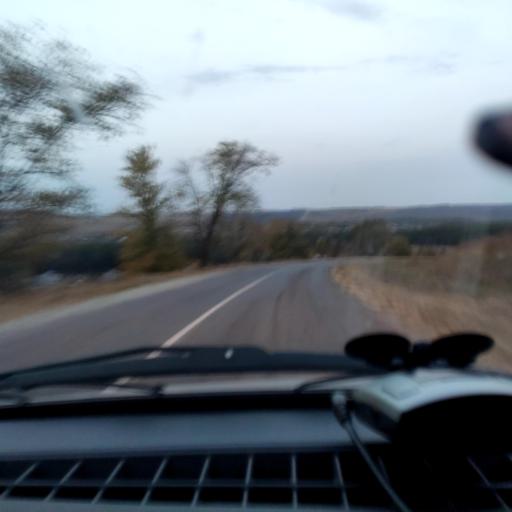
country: RU
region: Voronezj
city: Uryv-Pokrovka
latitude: 51.2228
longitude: 38.8987
